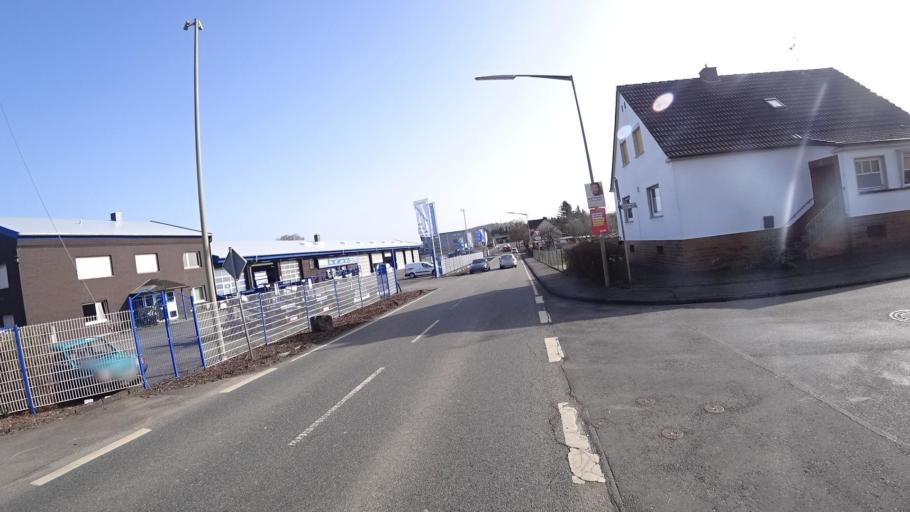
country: DE
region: Rheinland-Pfalz
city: Roth
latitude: 50.7674
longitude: 7.7015
